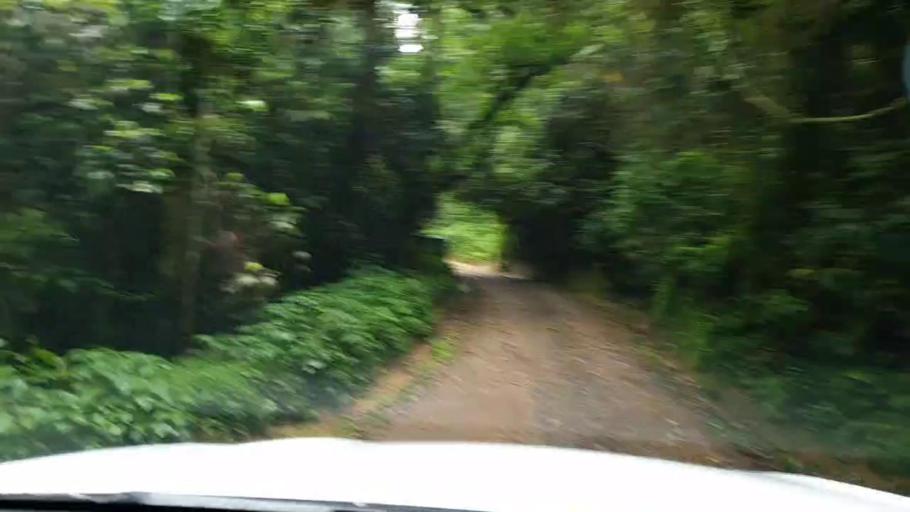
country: RW
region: Western Province
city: Cyangugu
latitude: -2.5581
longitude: 28.9810
